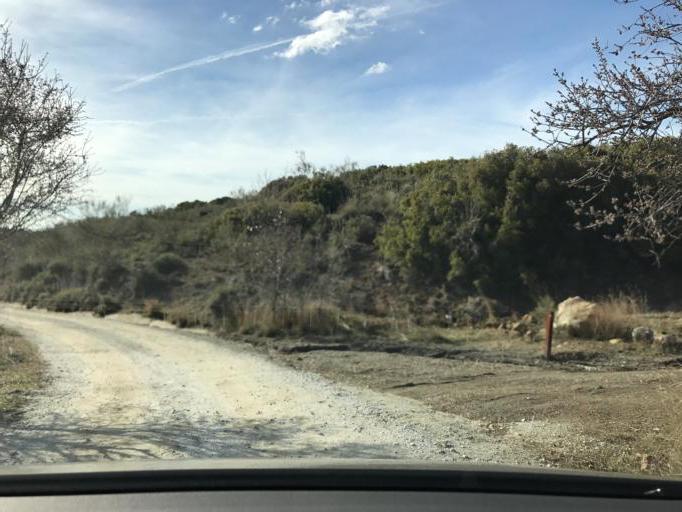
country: ES
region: Andalusia
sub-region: Provincia de Granada
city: Huetor Santillan
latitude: 37.2237
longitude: -3.4997
